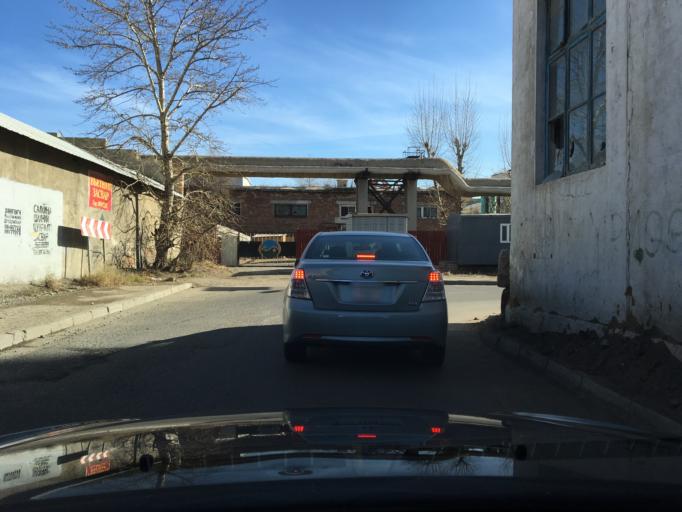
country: MN
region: Ulaanbaatar
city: Ulaanbaatar
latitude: 47.8941
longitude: 106.8966
